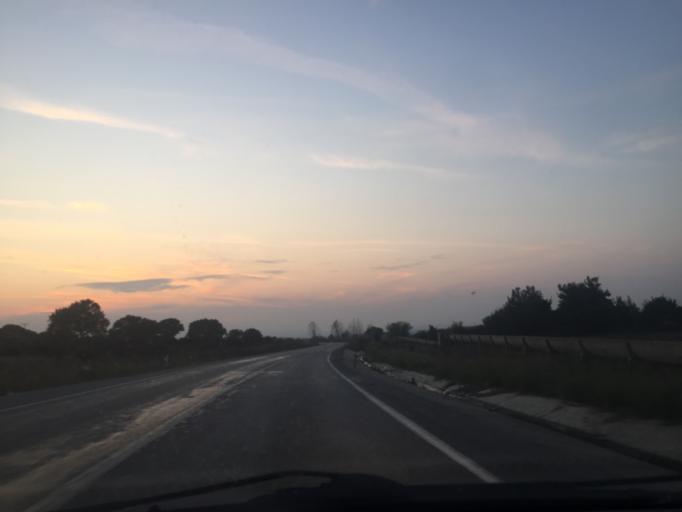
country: TR
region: Canakkale
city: Bayramic
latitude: 39.7872
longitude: 26.5282
